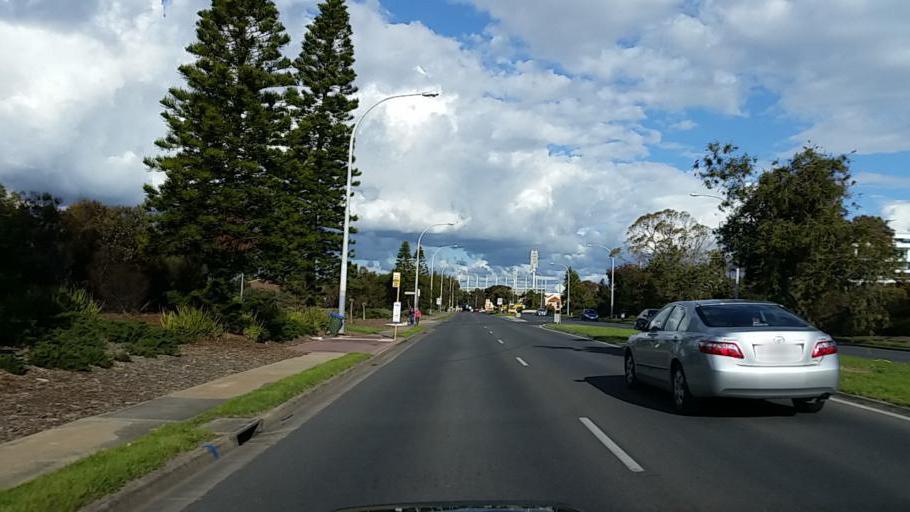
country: AU
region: South Australia
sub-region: Charles Sturt
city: West Lakes Shore
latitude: -34.8733
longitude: 138.4889
